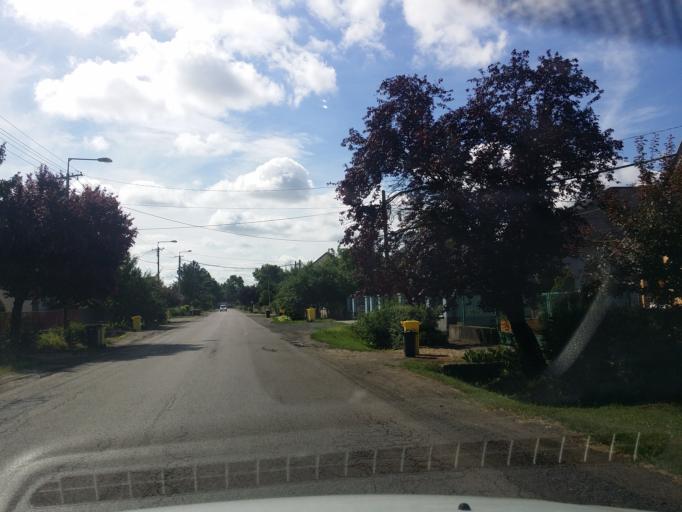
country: HU
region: Jasz-Nagykun-Szolnok
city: Jaszszentandras
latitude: 47.6492
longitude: 20.1577
